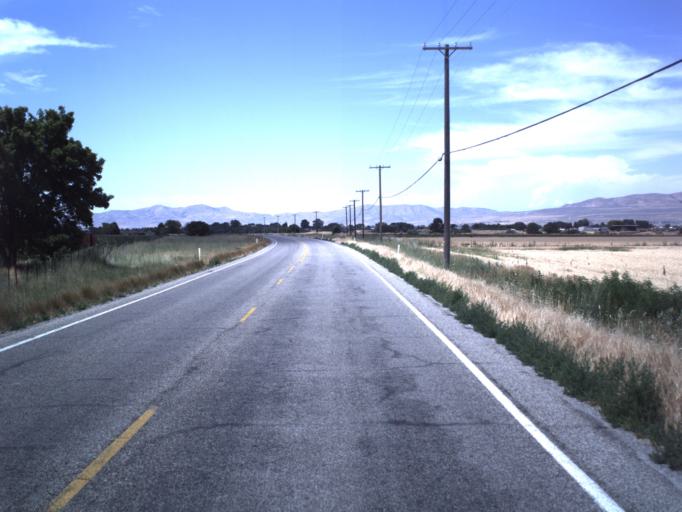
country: US
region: Utah
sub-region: Box Elder County
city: Elwood
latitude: 41.7153
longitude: -112.1014
